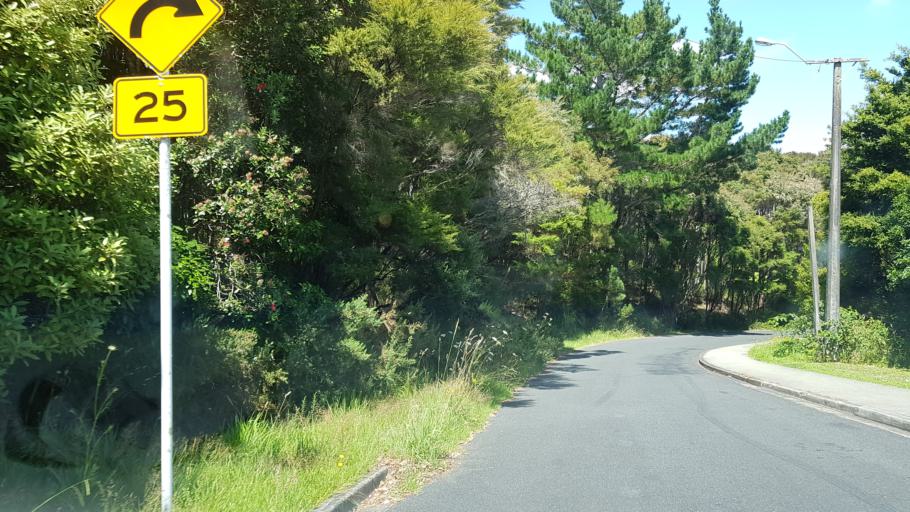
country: NZ
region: Auckland
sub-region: Auckland
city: North Shore
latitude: -36.7936
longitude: 174.7206
